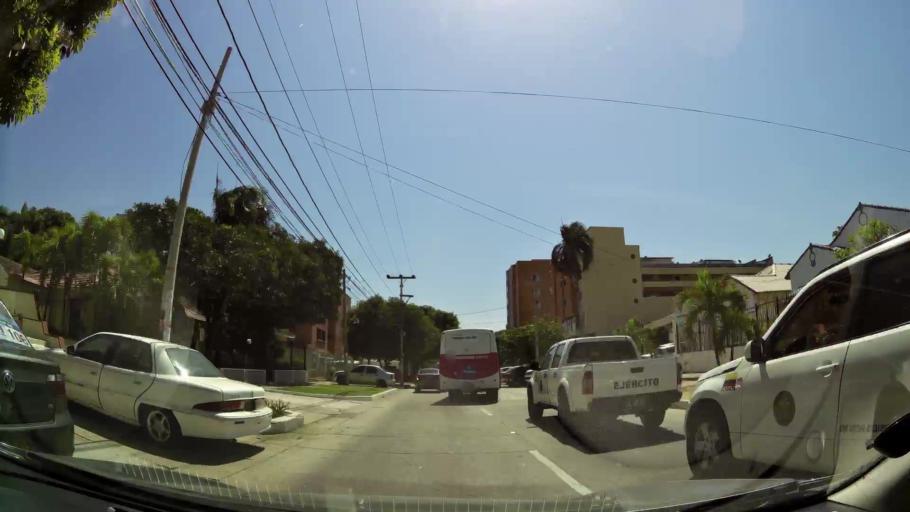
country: CO
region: Atlantico
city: Barranquilla
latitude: 11.0025
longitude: -74.7980
